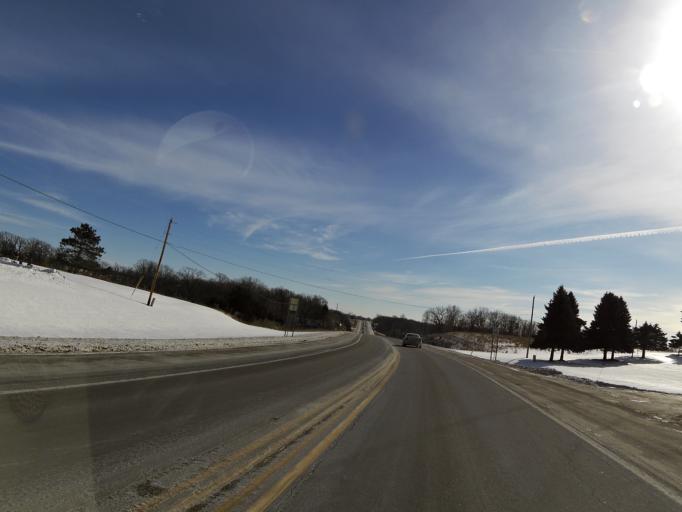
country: US
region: Minnesota
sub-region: Dakota County
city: Hastings
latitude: 44.7629
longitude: -92.8509
